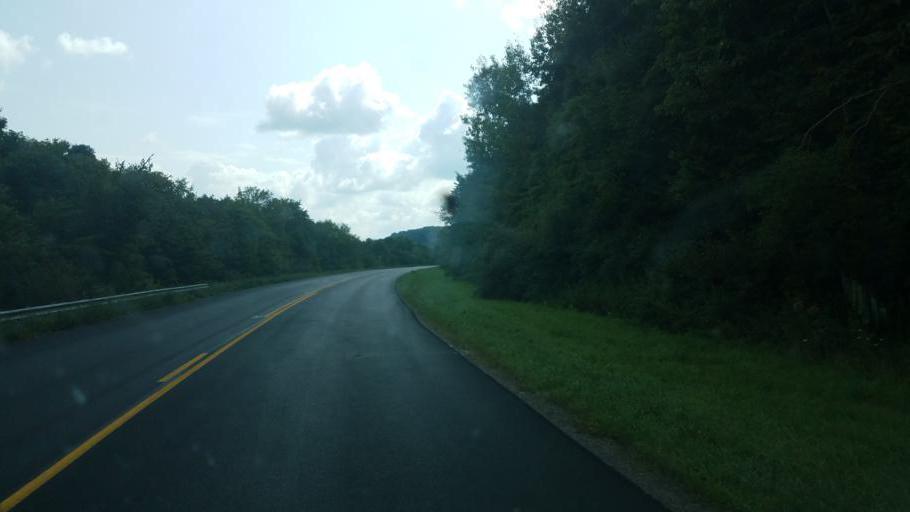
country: US
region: Ohio
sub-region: Columbiana County
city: New Waterford
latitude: 40.7970
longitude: -80.6506
